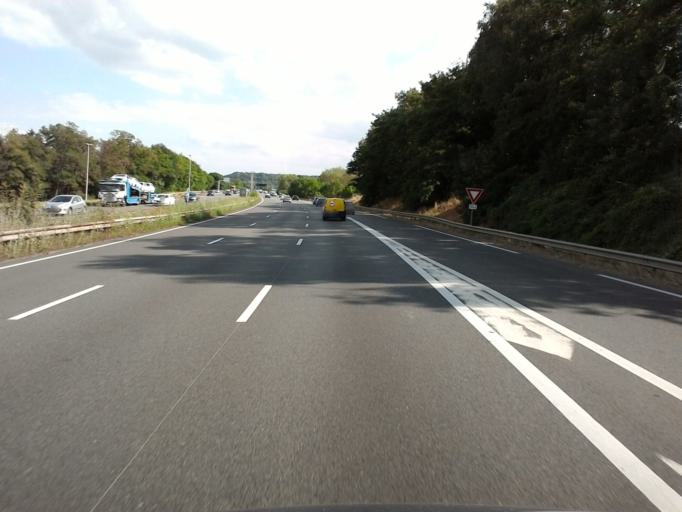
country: FR
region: Lorraine
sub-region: Departement de Meurthe-et-Moselle
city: Champigneulles
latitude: 48.7412
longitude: 6.1531
